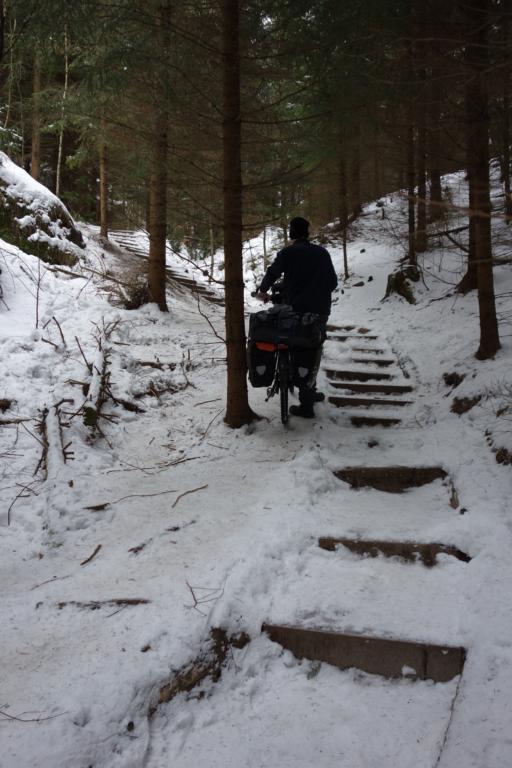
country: DE
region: Saxony
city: Bad Schandau
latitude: 50.9157
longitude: 14.1994
